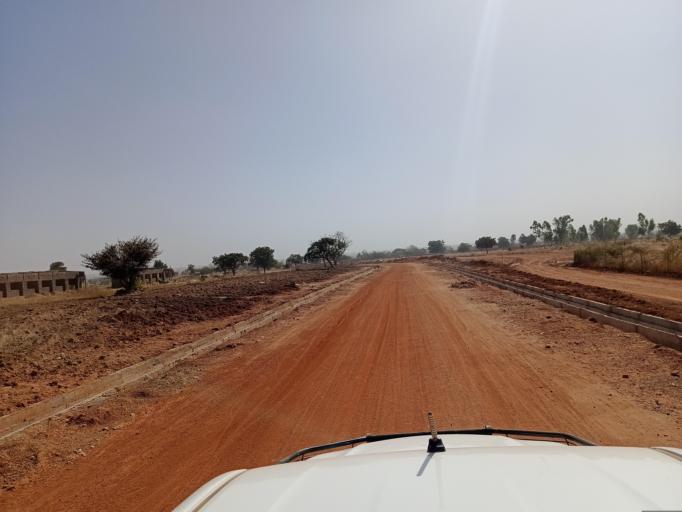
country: BF
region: Centre-Est
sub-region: Province du Boulgou
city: Garango
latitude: 11.5011
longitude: -0.5134
